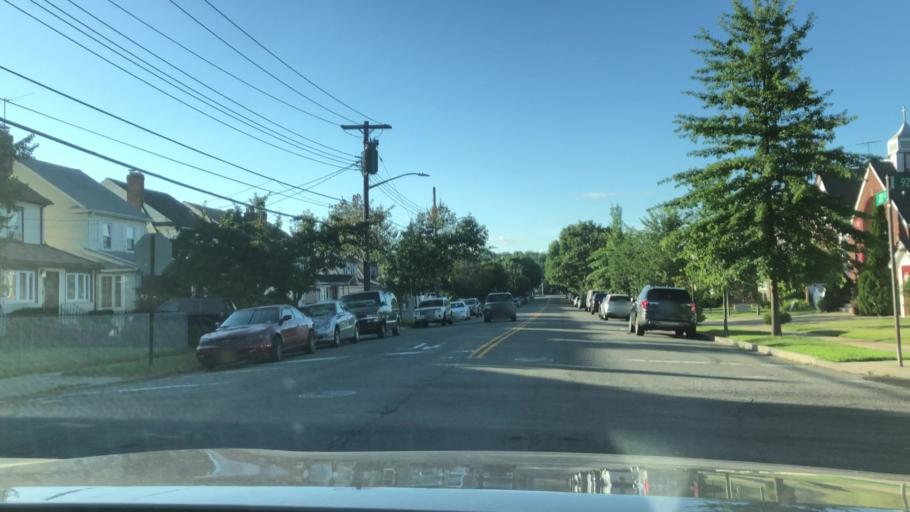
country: US
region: New York
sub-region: Nassau County
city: Bellerose Terrace
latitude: 40.7228
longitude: -73.7422
